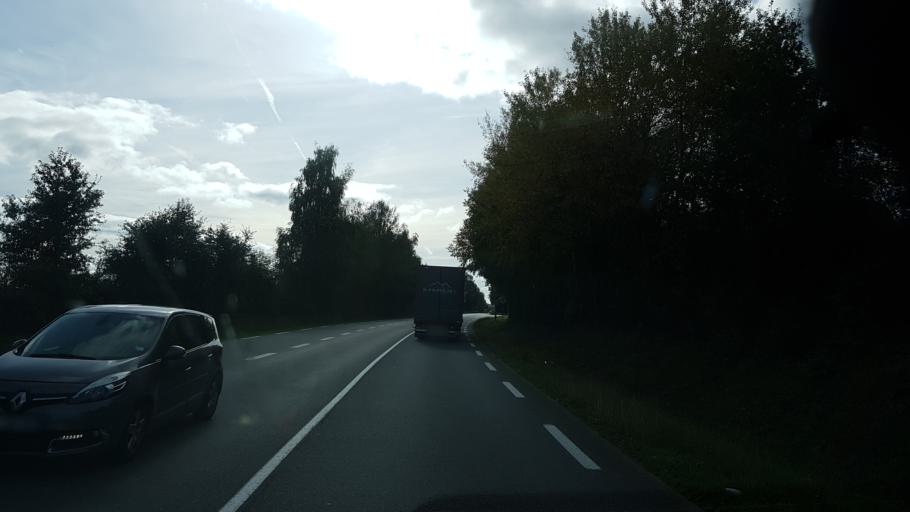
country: FR
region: Poitou-Charentes
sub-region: Departement de la Charente
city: Confolens
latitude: 46.0268
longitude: 0.6573
